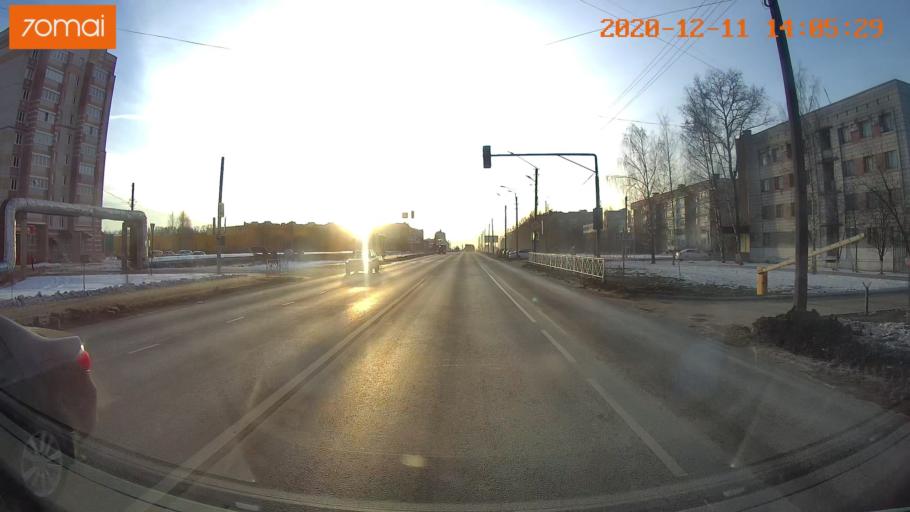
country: RU
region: Kostroma
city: Oktyabr'skiy
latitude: 57.7475
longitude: 41.0125
